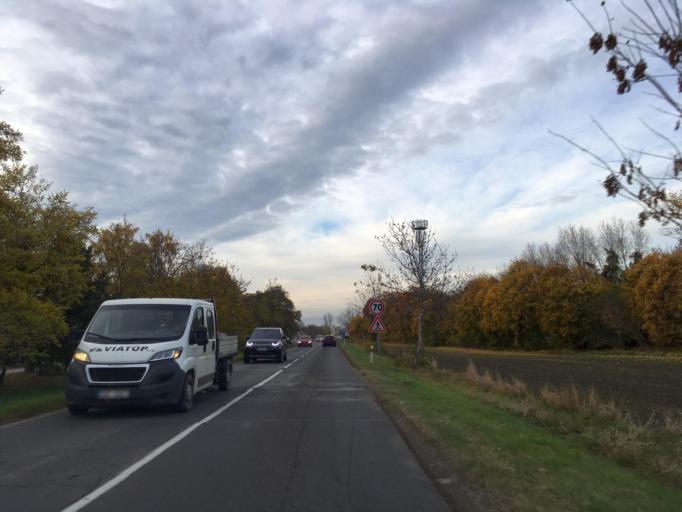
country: SK
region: Trnavsky
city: Dunajska Streda
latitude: 48.0113
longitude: 17.5830
